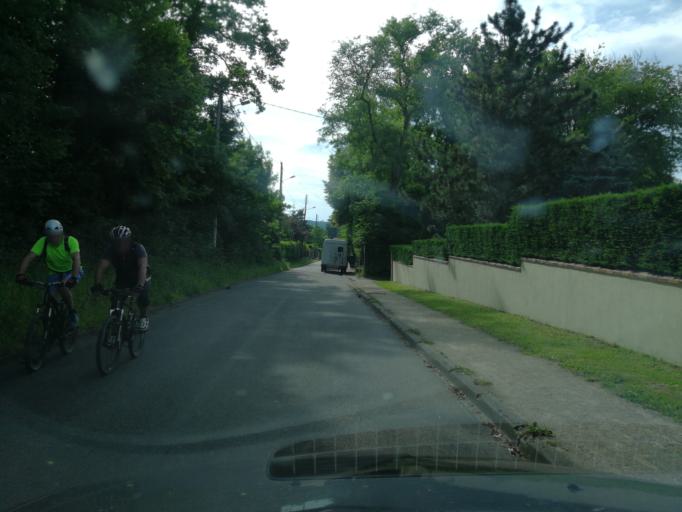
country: FR
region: Ile-de-France
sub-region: Departement des Yvelines
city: Saint-Remy-les-Chevreuse
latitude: 48.7004
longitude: 2.0756
